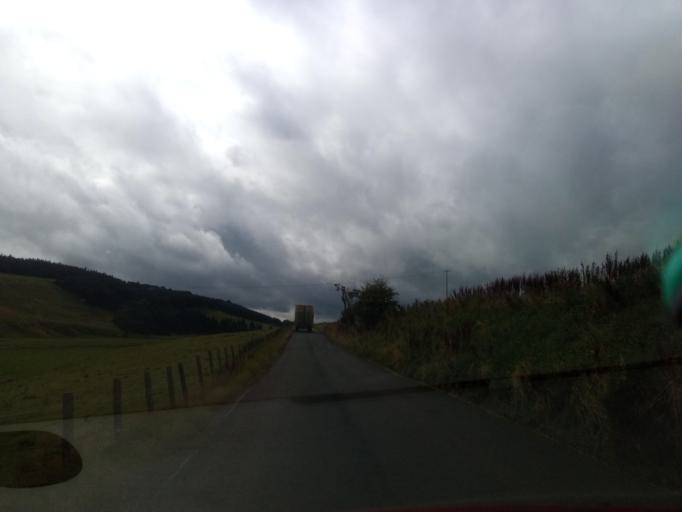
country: GB
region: Scotland
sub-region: The Scottish Borders
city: Duns
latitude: 55.8316
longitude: -2.4433
